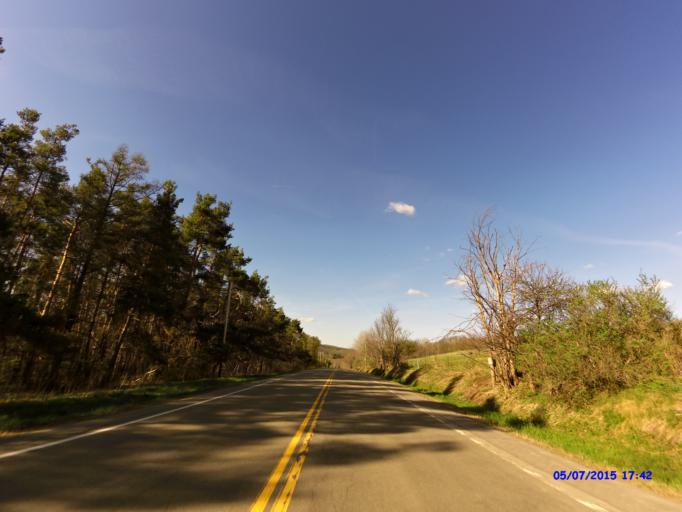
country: US
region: New York
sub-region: Cattaraugus County
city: Franklinville
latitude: 42.3019
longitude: -78.5118
